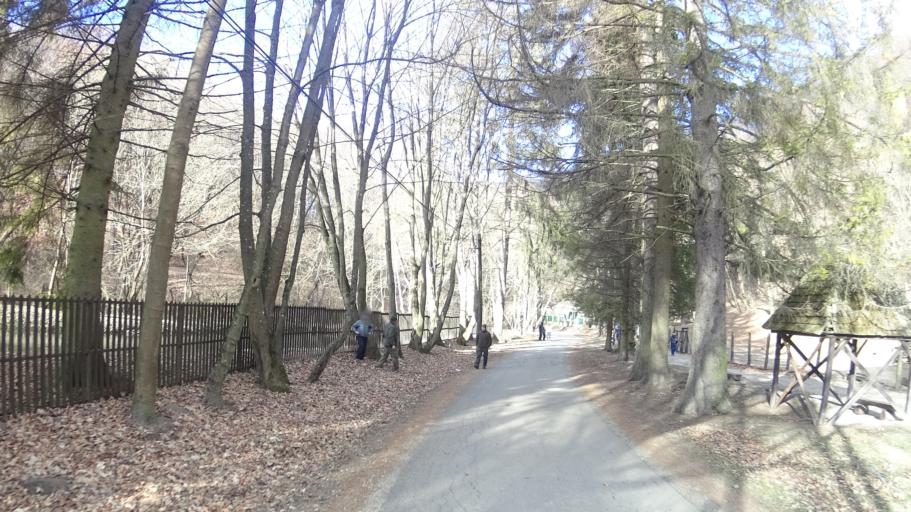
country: HU
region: Heves
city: Szilvasvarad
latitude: 48.0870
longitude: 20.4065
